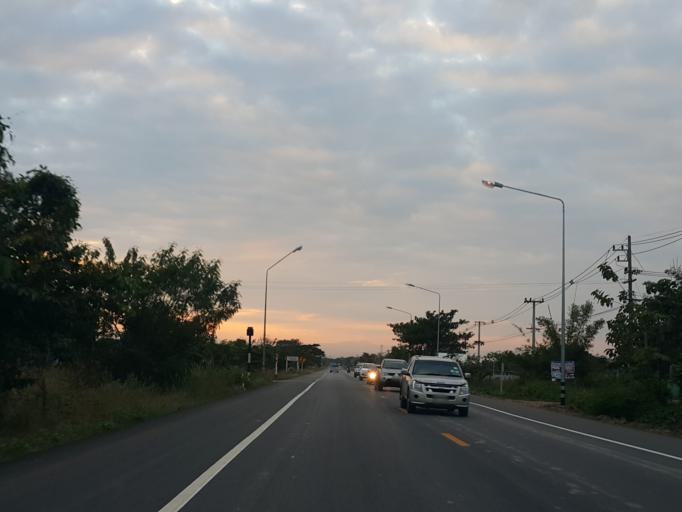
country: TH
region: Lampang
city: Lampang
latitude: 18.2513
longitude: 99.5137
